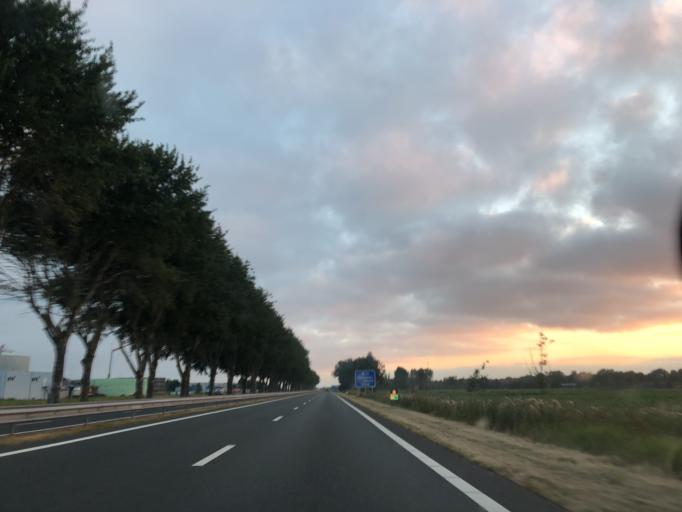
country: NL
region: Groningen
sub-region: Gemeente Veendam
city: Veendam
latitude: 53.1174
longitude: 6.8995
